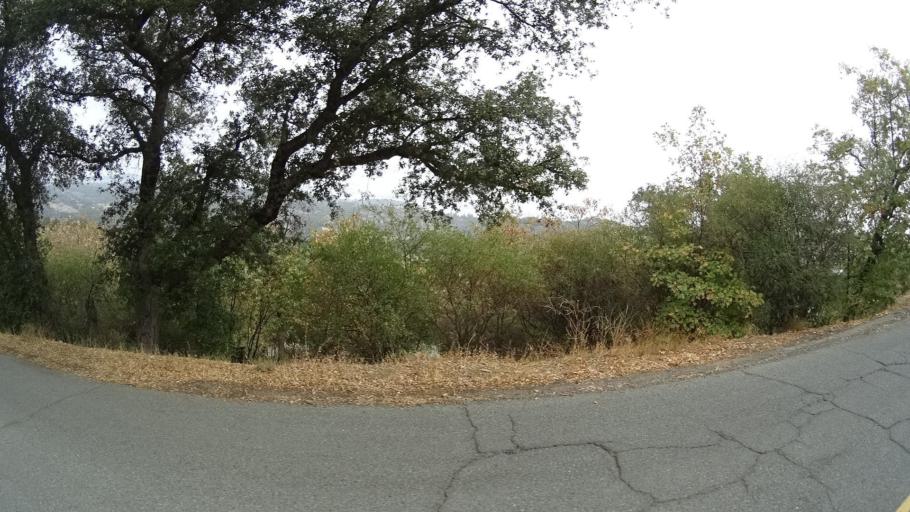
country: US
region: California
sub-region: San Diego County
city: Julian
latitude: 33.0587
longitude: -116.6056
